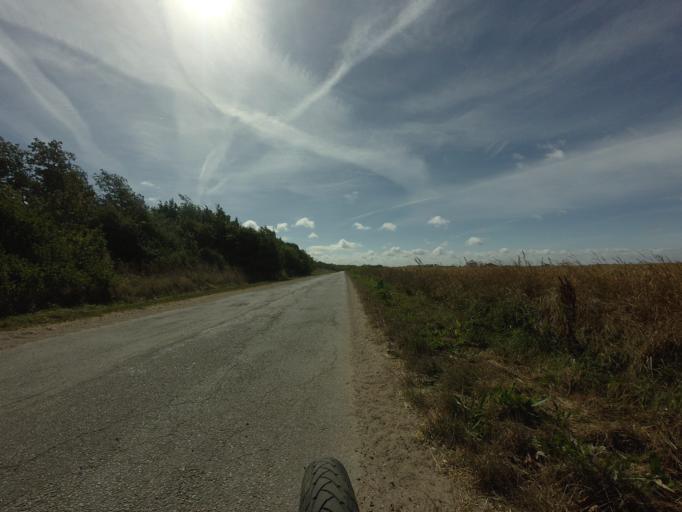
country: DK
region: North Denmark
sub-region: Hjorring Kommune
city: Vra
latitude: 57.3388
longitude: 9.8092
